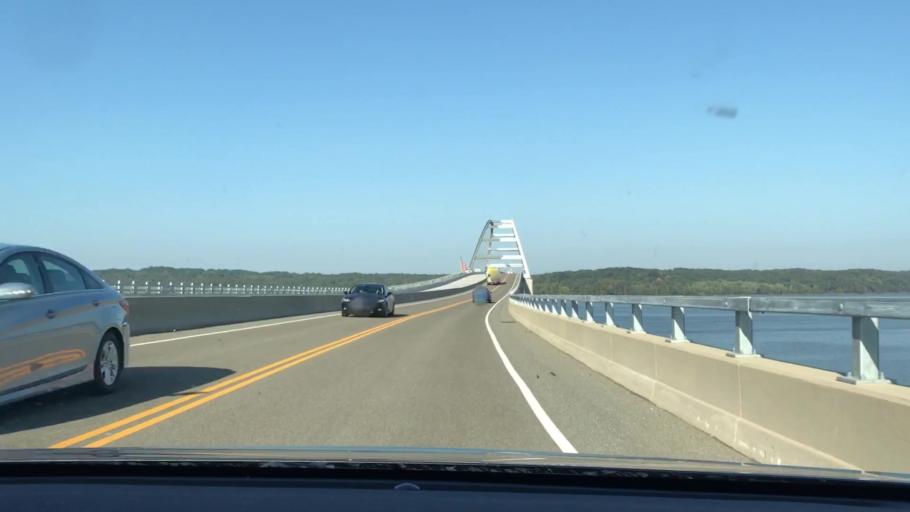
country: US
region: Kentucky
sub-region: Trigg County
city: Cadiz
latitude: 36.7986
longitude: -87.9705
